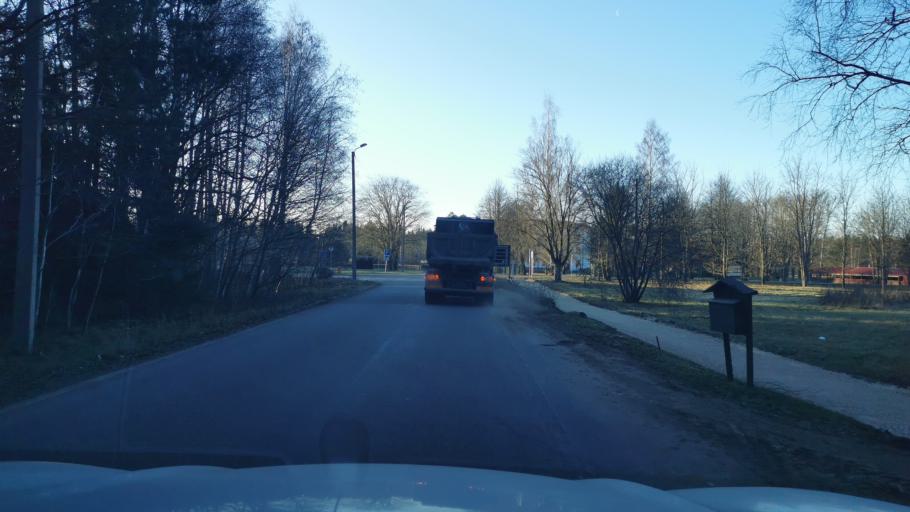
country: EE
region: Ida-Virumaa
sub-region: Kohtla-Nomme vald
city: Kohtla-Nomme
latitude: 59.3512
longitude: 27.1767
